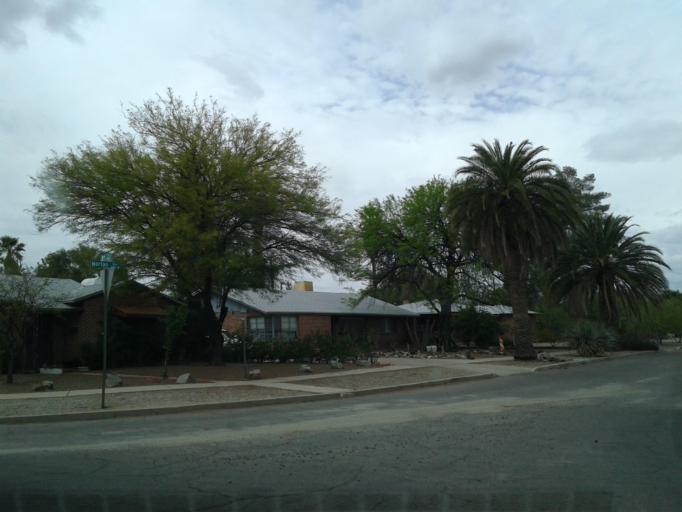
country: US
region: Arizona
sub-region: Pima County
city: Tucson
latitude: 32.2240
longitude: -110.9361
